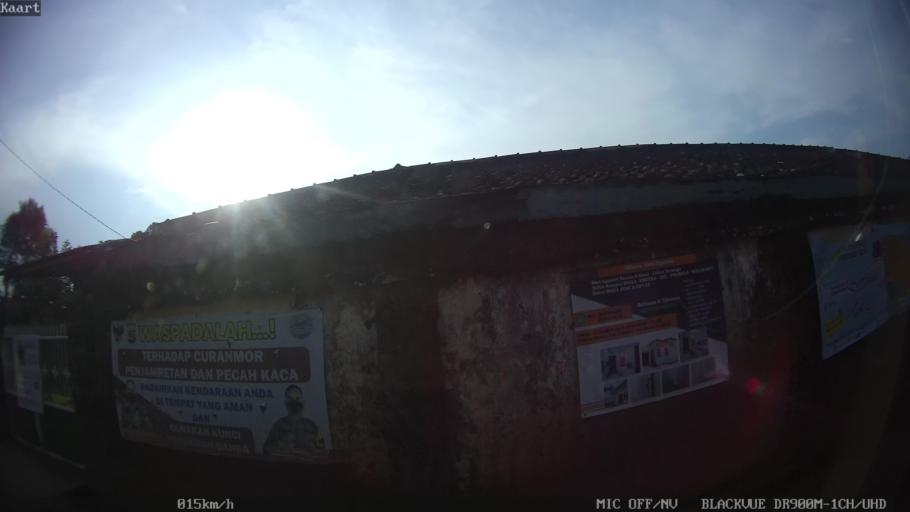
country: ID
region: Lampung
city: Kedaton
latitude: -5.3757
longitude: 105.2419
